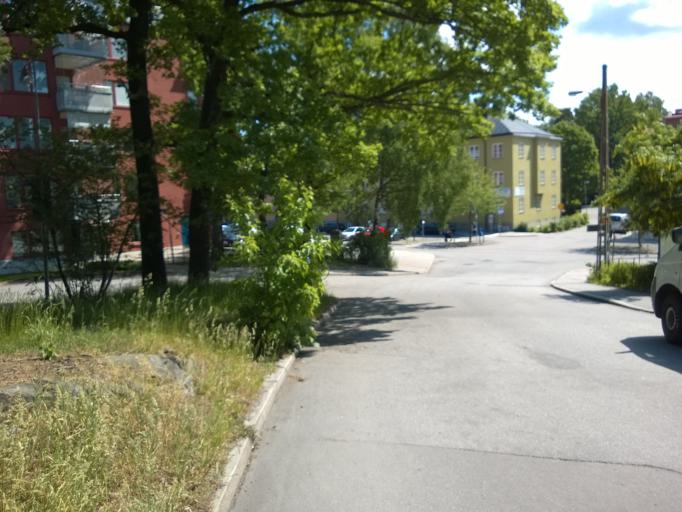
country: SE
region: Stockholm
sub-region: Solna Kommun
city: Solna
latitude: 59.3662
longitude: 17.9991
